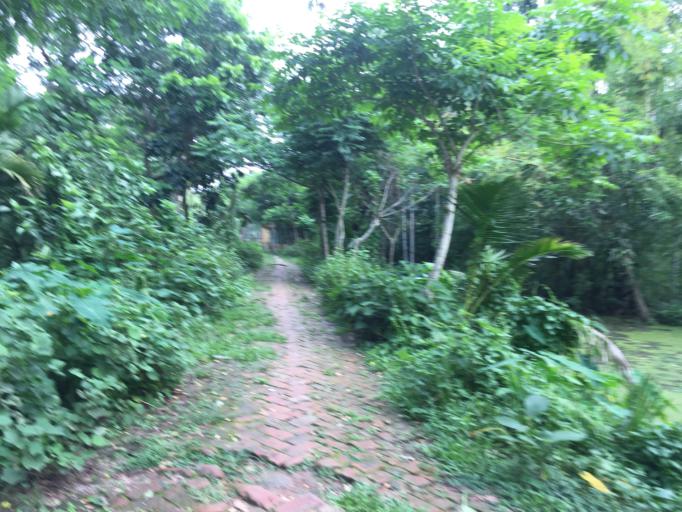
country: BD
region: Barisal
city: Mathba
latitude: 22.1897
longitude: 89.9249
